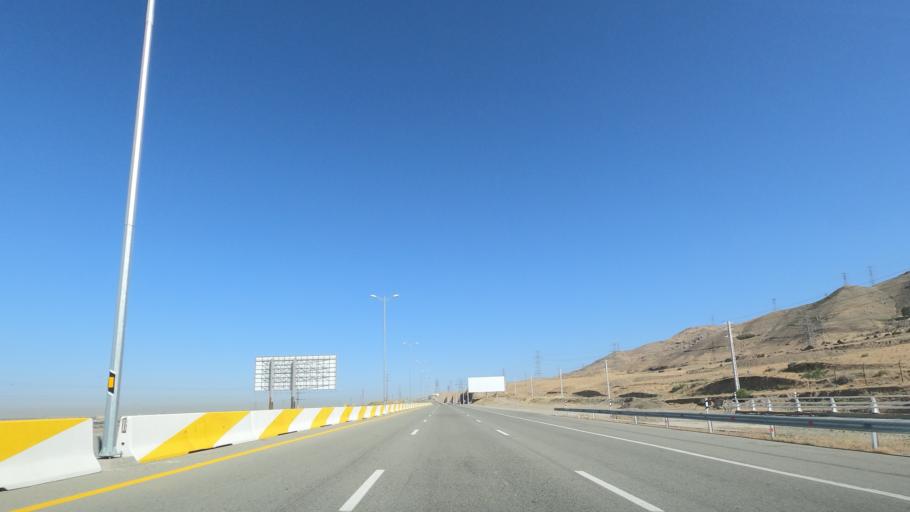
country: IR
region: Tehran
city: Shahr-e Qods
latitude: 35.7693
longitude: 51.0624
